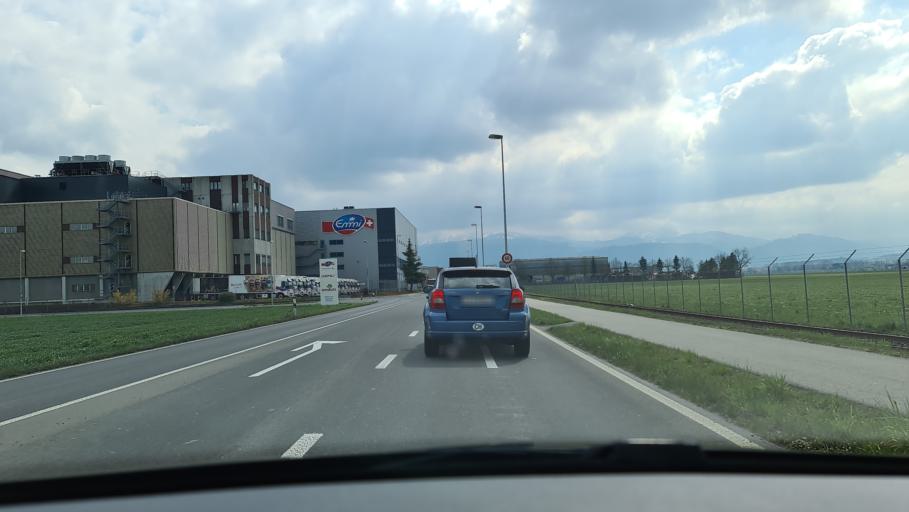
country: CH
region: Lucerne
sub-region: Lucerne-Land District
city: Ebikon
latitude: 47.0977
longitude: 8.3152
